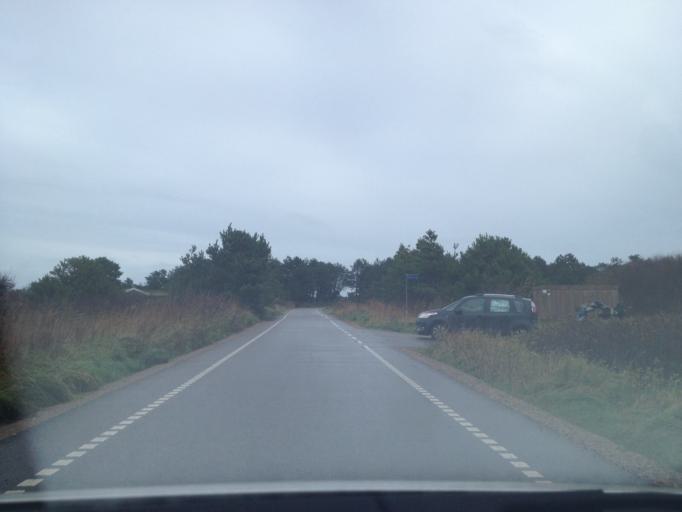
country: DE
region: Schleswig-Holstein
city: List
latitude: 55.1560
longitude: 8.5157
